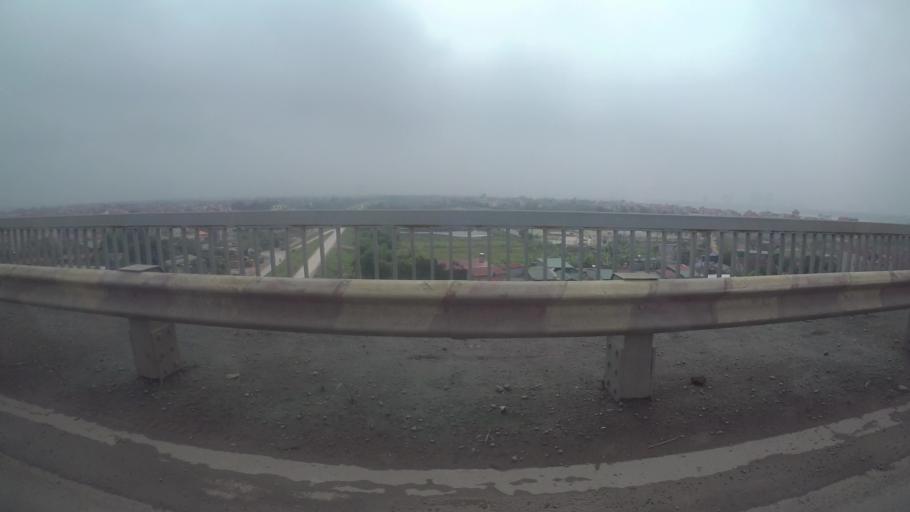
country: VN
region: Ha Noi
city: Tay Ho
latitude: 21.1062
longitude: 105.7871
